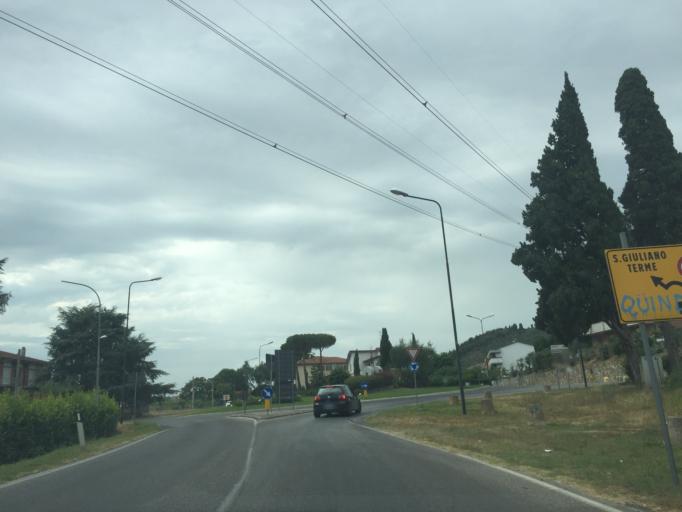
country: IT
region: Tuscany
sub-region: Province of Pisa
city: Gabella
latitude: 43.7225
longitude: 10.5009
